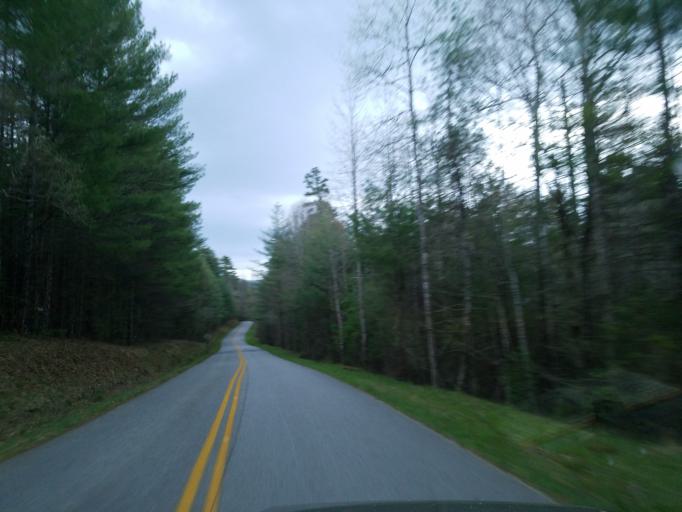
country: US
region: Georgia
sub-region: Union County
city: Blairsville
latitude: 34.7615
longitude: -84.1142
